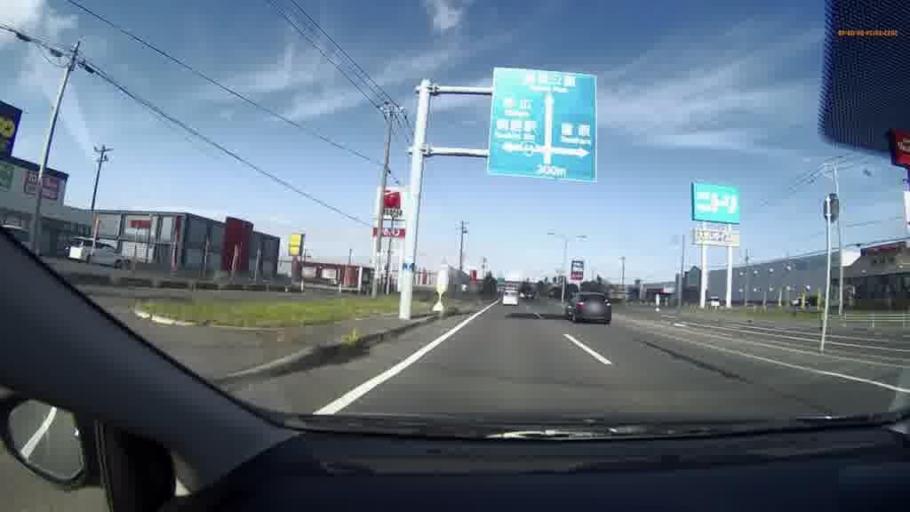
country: JP
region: Hokkaido
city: Kushiro
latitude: 43.0087
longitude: 144.4123
